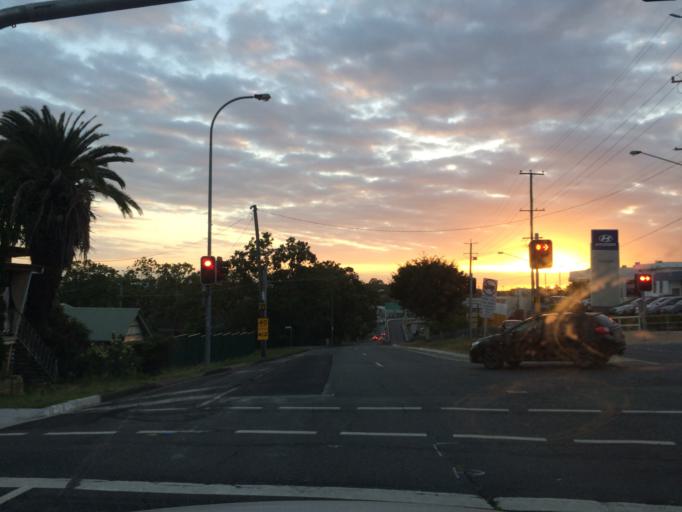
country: AU
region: Queensland
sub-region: Brisbane
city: Taringa
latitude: -27.4980
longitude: 152.9703
